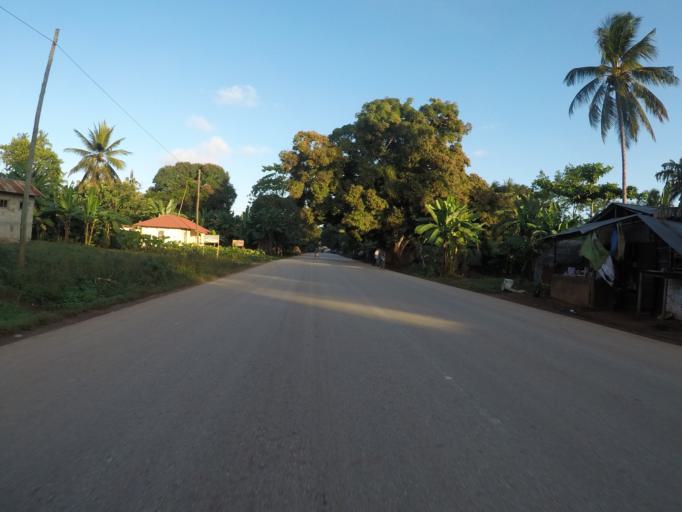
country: TZ
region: Zanzibar North
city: Gamba
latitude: -5.8820
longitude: 39.2835
